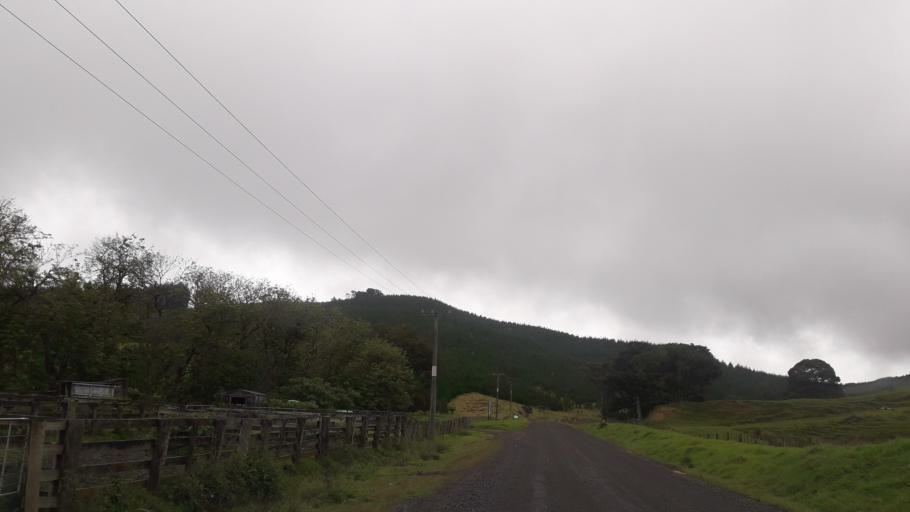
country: NZ
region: Northland
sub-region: Far North District
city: Ahipara
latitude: -35.4346
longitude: 173.3431
